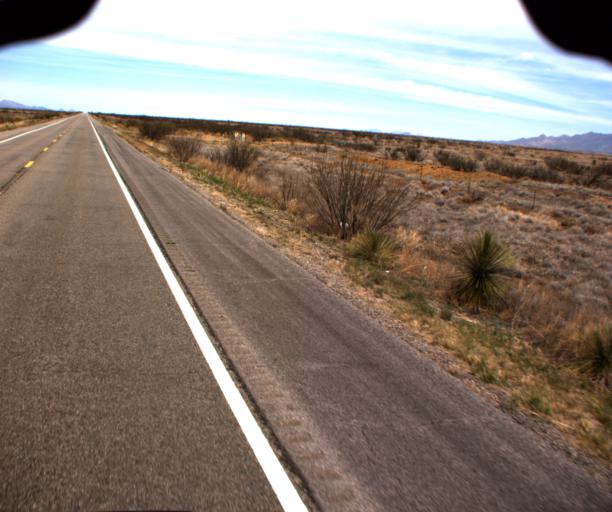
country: US
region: Arizona
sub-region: Cochise County
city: Pirtleville
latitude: 31.4936
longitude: -109.6314
